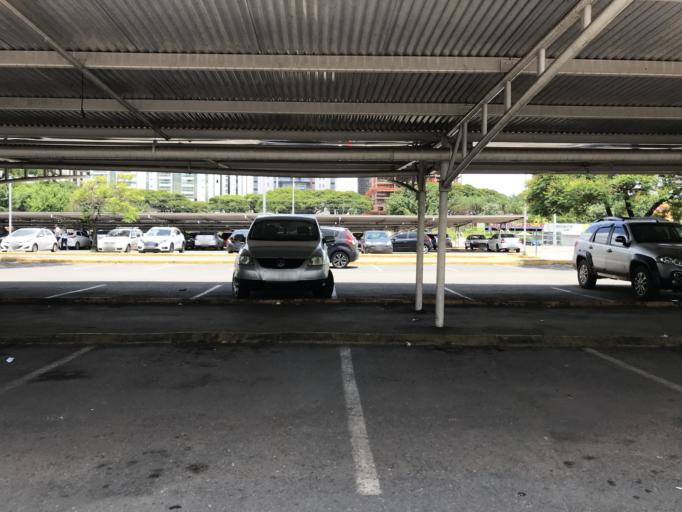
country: BR
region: Federal District
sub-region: Brasilia
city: Brasilia
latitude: -15.8308
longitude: -47.9540
